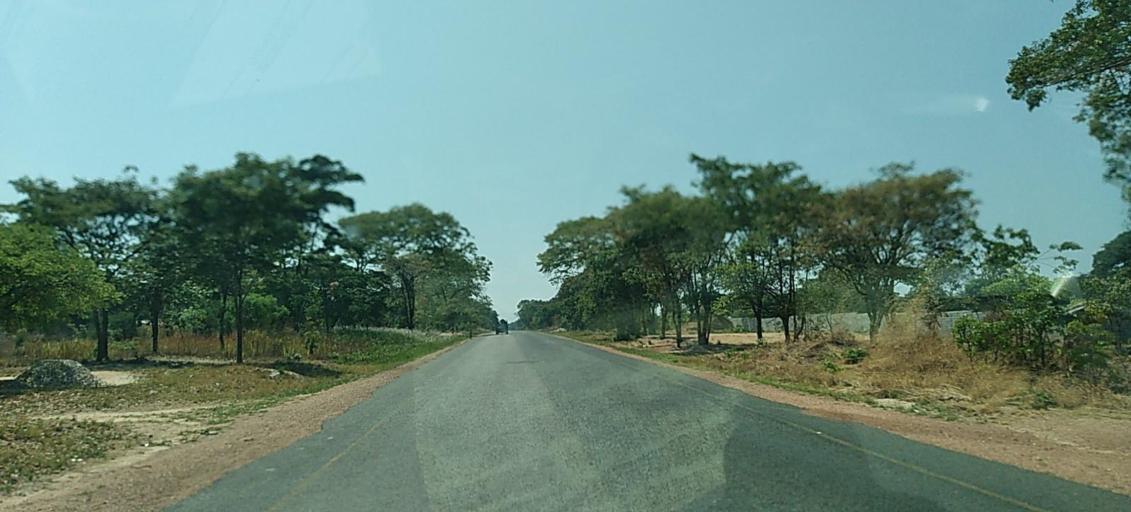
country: ZM
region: North-Western
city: Solwezi
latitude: -12.2937
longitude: 25.8181
